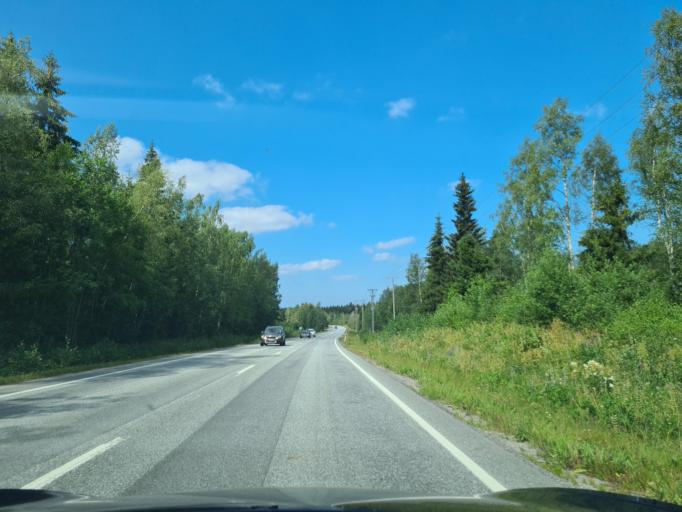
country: FI
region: Ostrobothnia
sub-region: Vaasa
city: Vaasa
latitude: 63.1855
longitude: 21.5669
